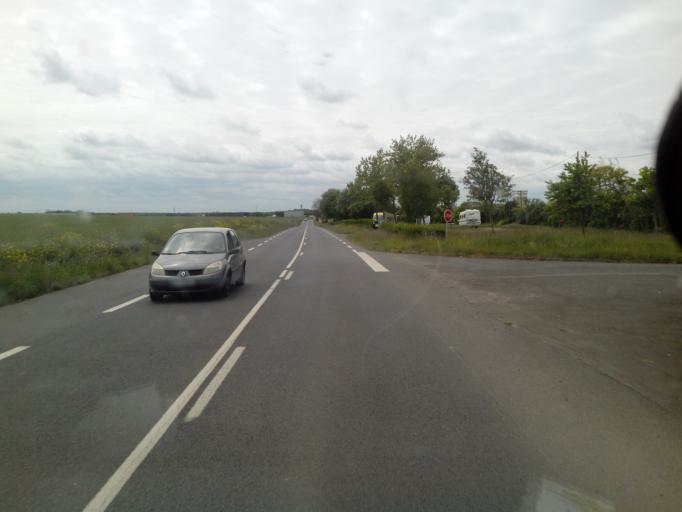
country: FR
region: Lower Normandy
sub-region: Departement du Calvados
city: Ranville
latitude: 49.2452
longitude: -0.2514
